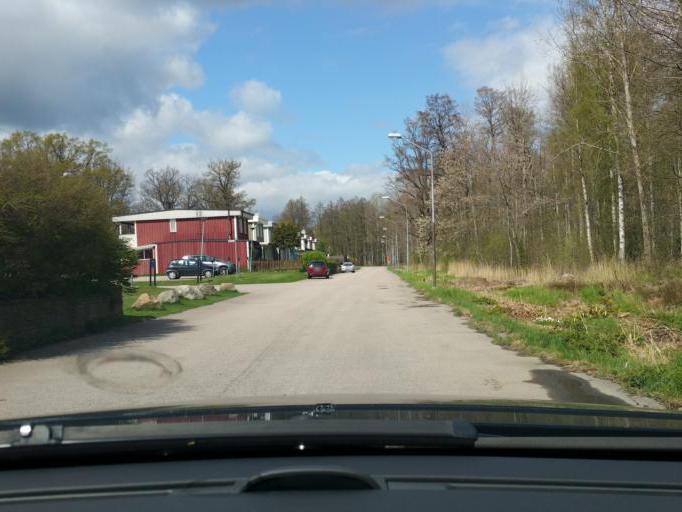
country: SE
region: Kronoberg
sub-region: Vaxjo Kommun
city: Lammhult
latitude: 57.1727
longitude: 14.5921
